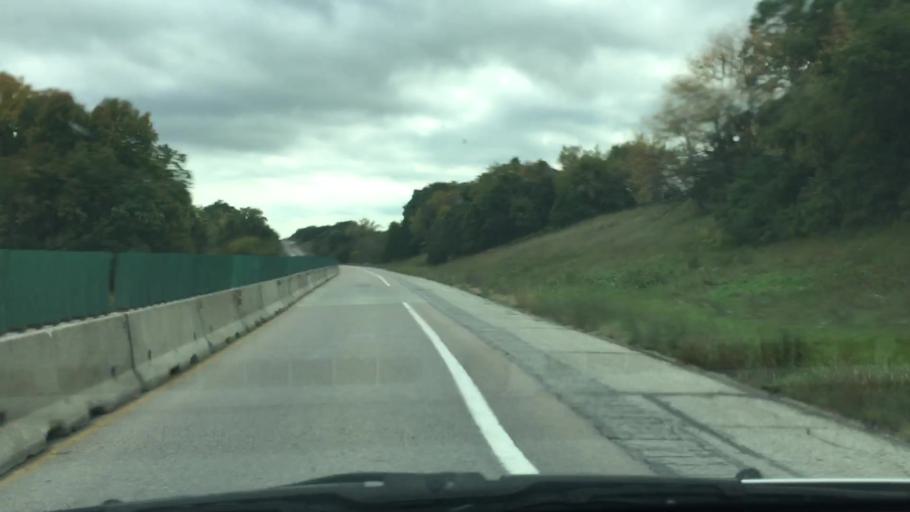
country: US
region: Iowa
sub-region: Decatur County
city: Leon
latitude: 40.7170
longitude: -93.8451
